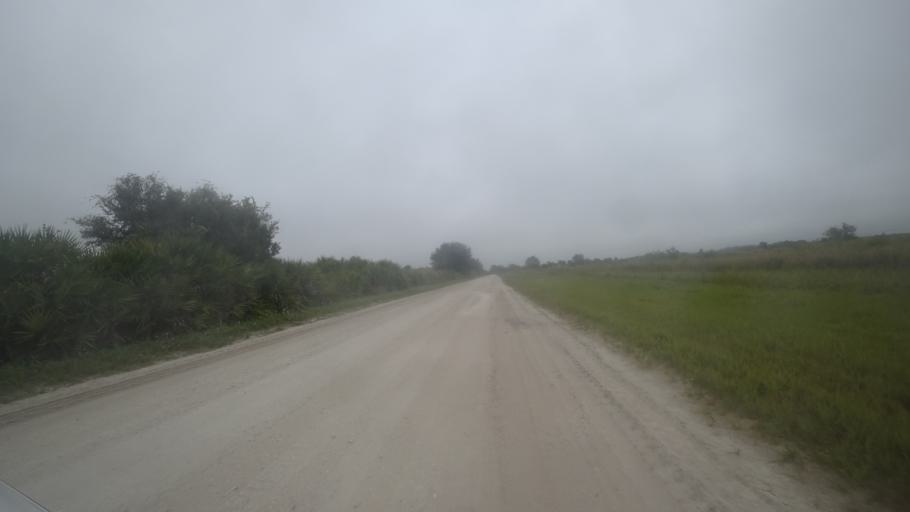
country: US
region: Florida
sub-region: Sarasota County
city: The Meadows
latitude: 27.4508
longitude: -82.3380
